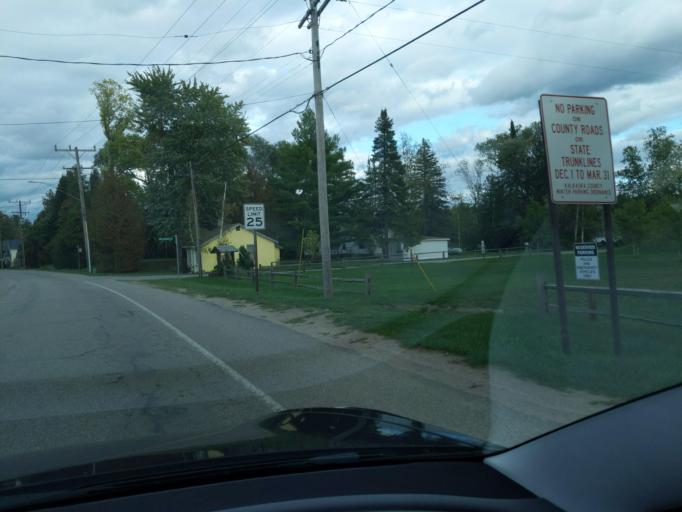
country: US
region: Michigan
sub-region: Kalkaska County
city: Rapid City
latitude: 44.8506
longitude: -85.3259
